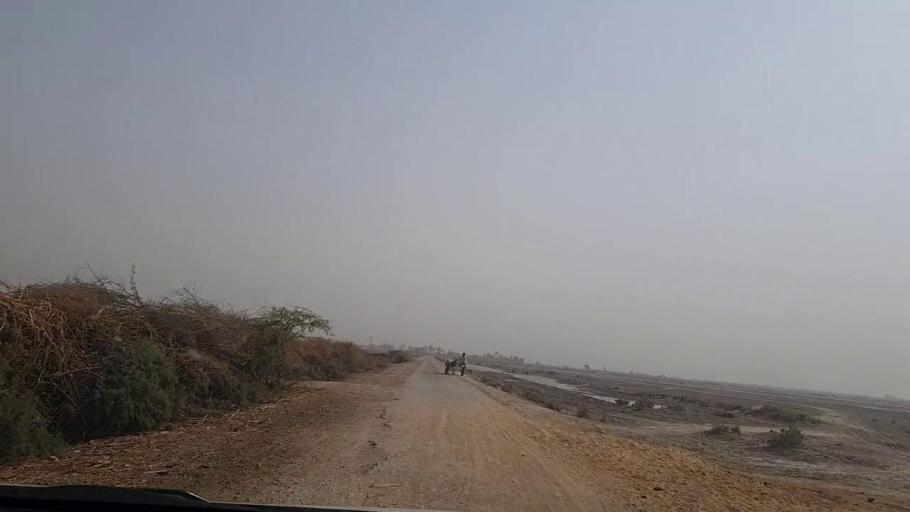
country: PK
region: Sindh
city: Pithoro
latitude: 25.4600
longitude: 69.2298
